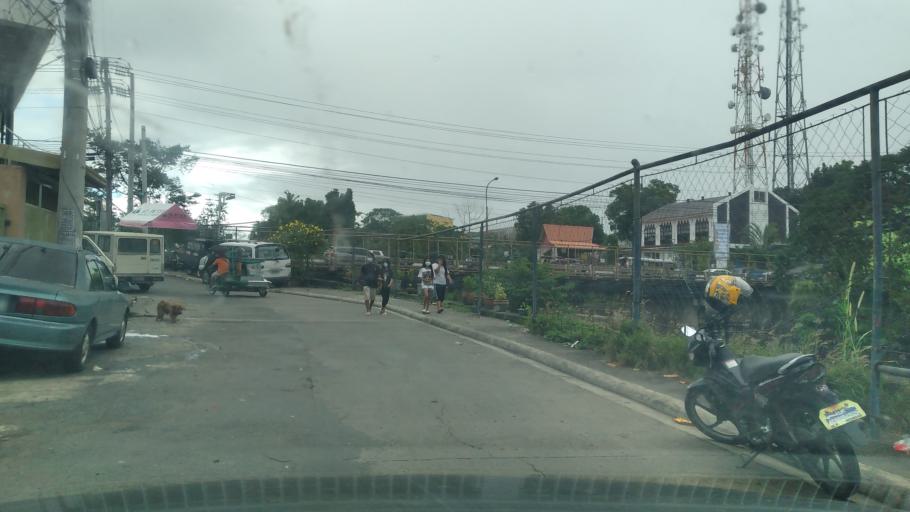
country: PH
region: Calabarzon
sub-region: Province of Quezon
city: Lucena
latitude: 13.9370
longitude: 121.6174
